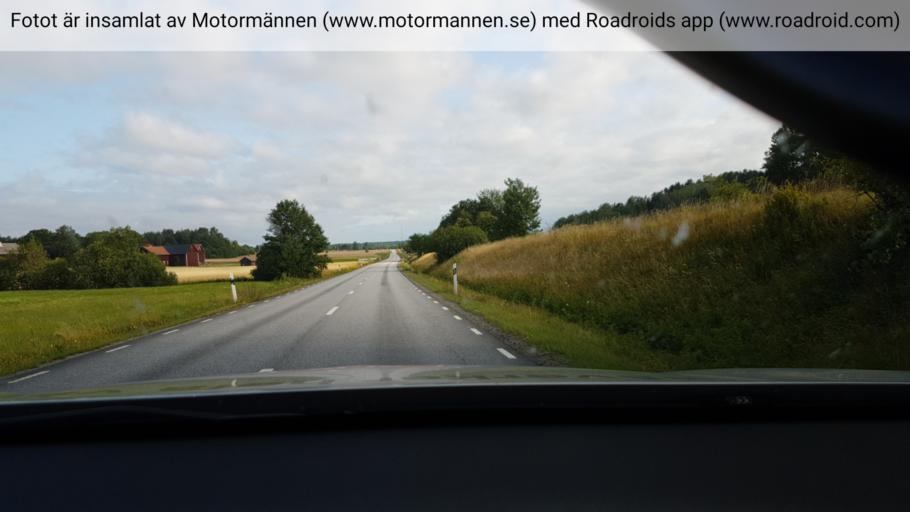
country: SE
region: Stockholm
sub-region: Norrtalje Kommun
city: Rimbo
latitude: 59.7203
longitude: 18.3738
